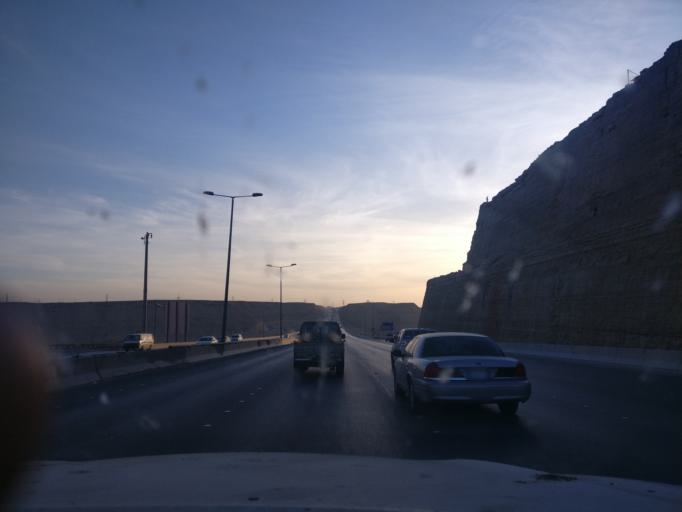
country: SA
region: Ar Riyad
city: Riyadh
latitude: 24.6180
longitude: 46.5714
